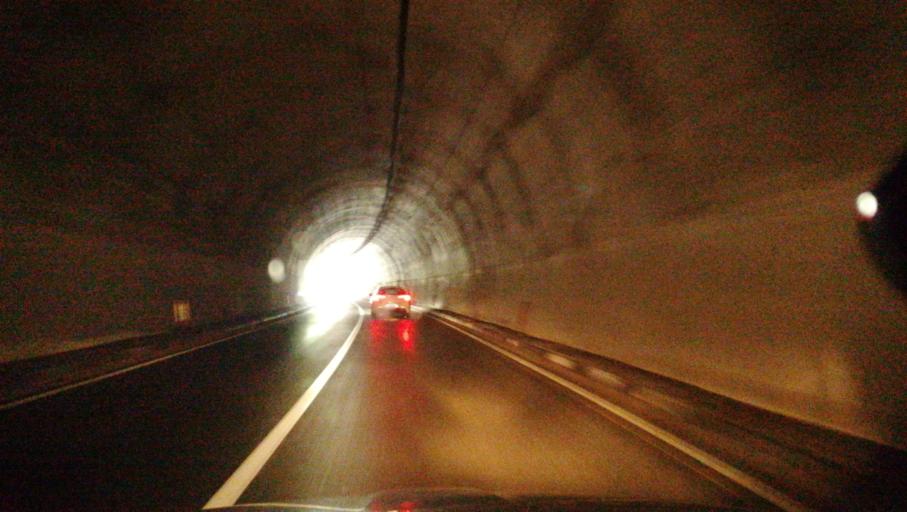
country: BA
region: Republika Srpska
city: Visegrad
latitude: 43.7514
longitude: 19.2280
